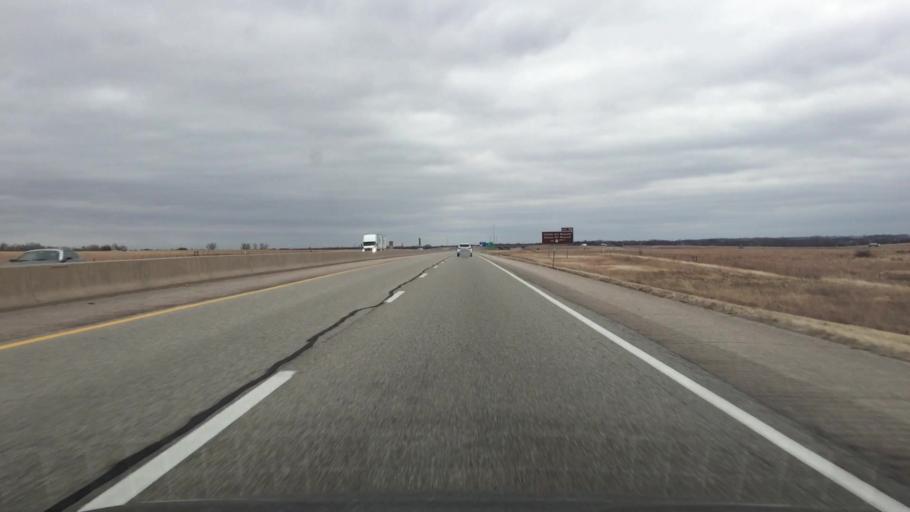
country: US
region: Kansas
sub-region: Butler County
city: El Dorado
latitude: 37.8866
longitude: -96.8398
